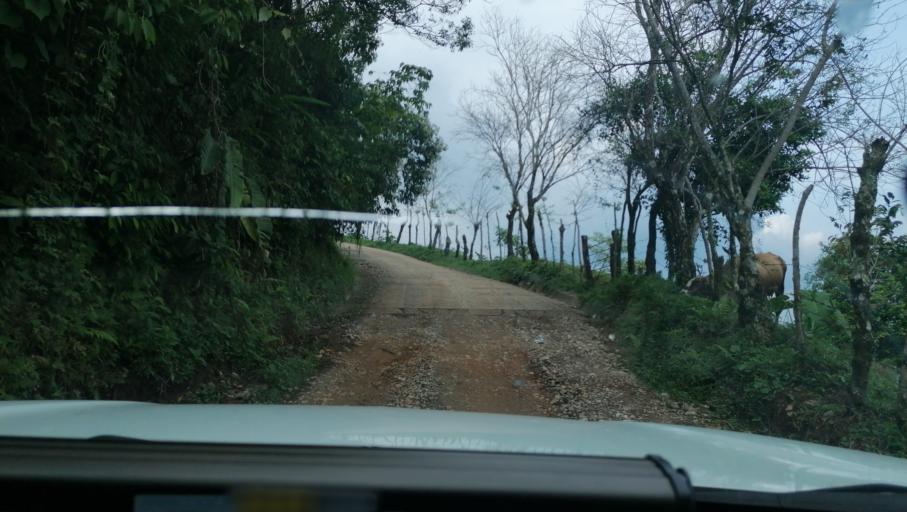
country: MX
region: Chiapas
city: Ixtacomitan
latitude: 17.3360
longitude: -93.1089
